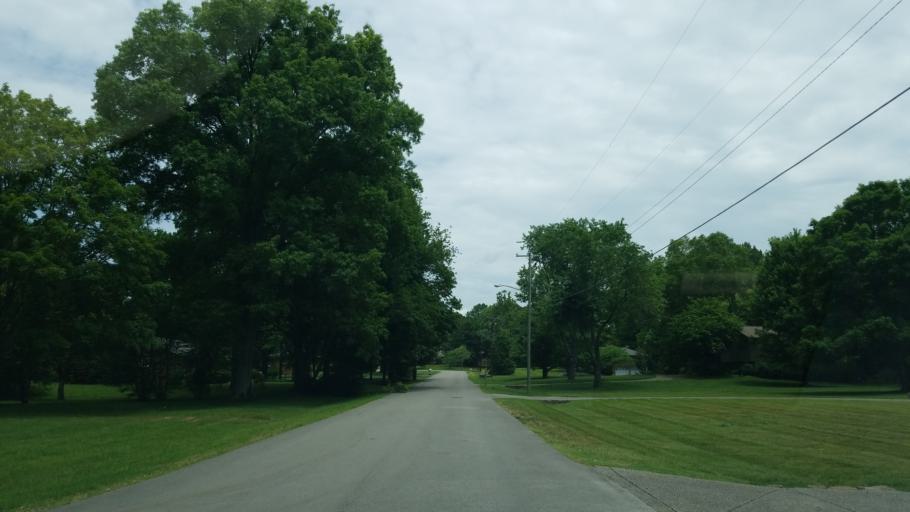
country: US
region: Tennessee
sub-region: Williamson County
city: Brentwood
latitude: 36.0298
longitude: -86.7935
